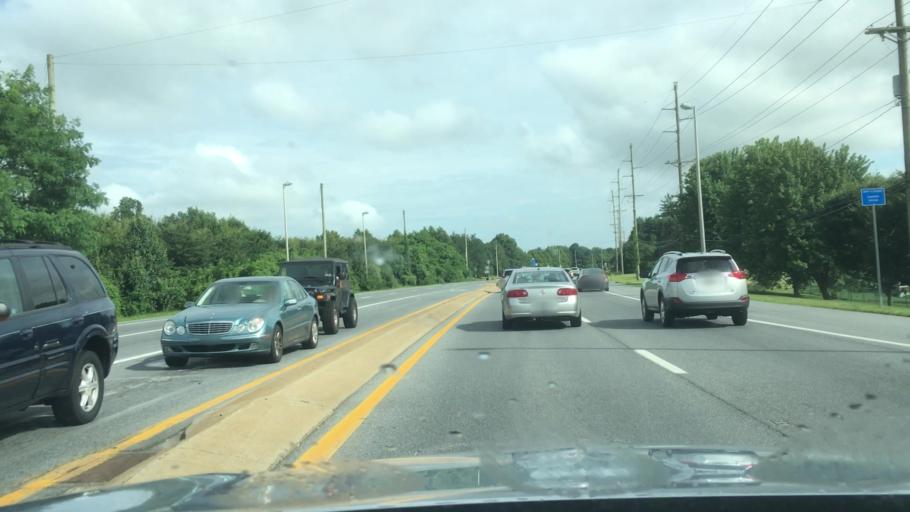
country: US
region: Delaware
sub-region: New Castle County
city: North Star
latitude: 39.7662
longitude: -75.7065
